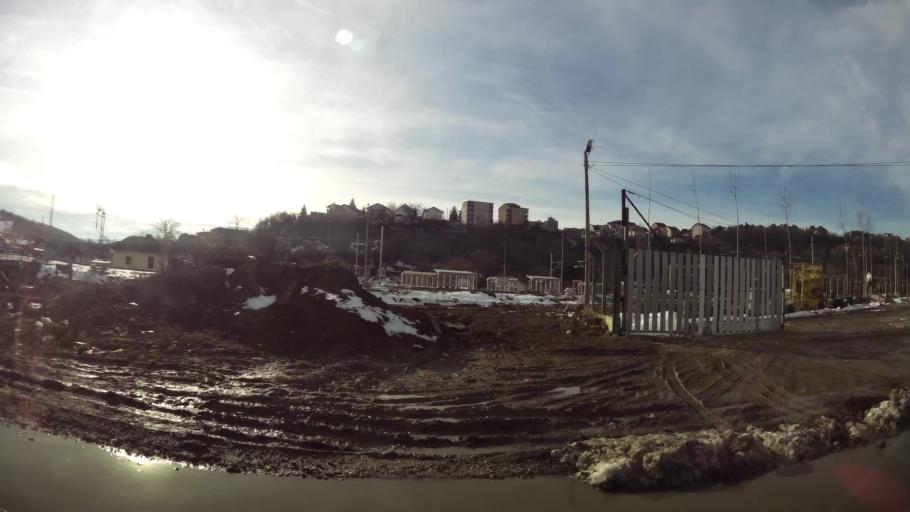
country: RS
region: Central Serbia
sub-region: Belgrade
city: Rakovica
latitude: 44.7237
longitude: 20.4376
